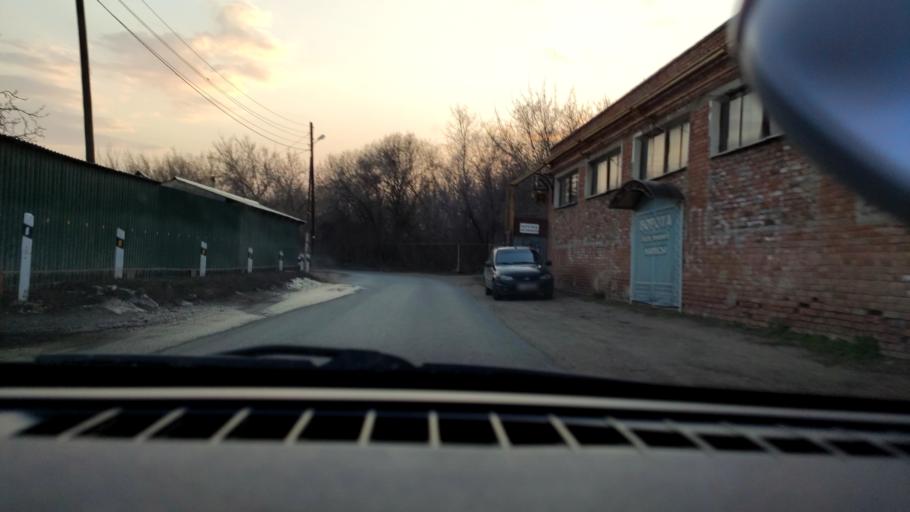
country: RU
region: Samara
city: Smyshlyayevka
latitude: 53.2082
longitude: 50.3227
